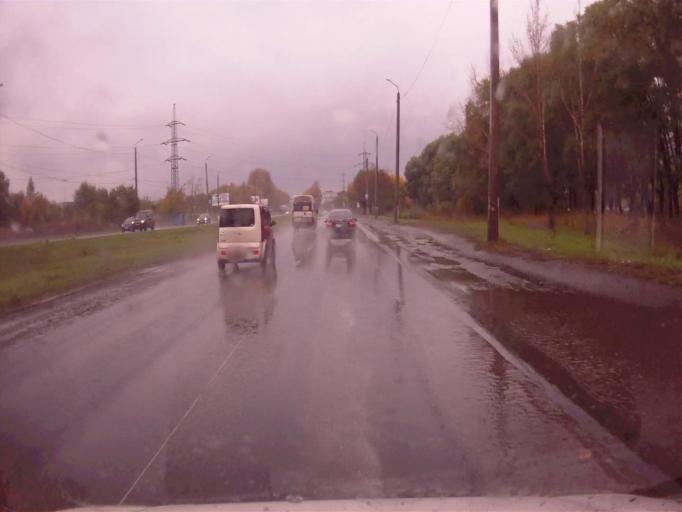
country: RU
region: Chelyabinsk
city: Dolgoderevenskoye
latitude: 55.2463
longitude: 61.3588
